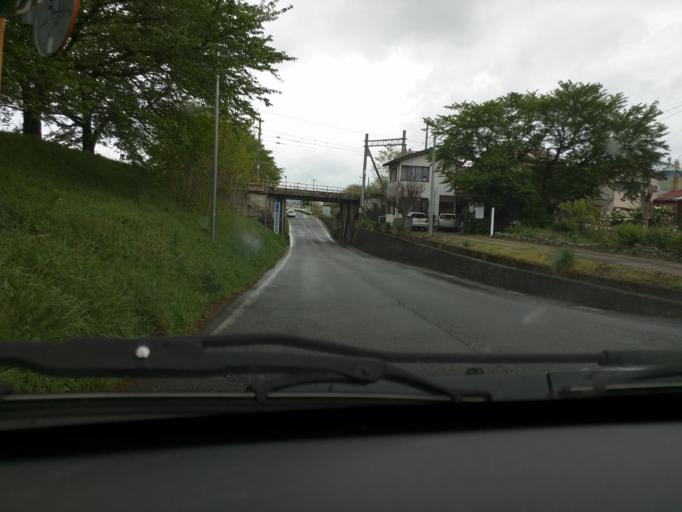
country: JP
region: Fukushima
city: Kitakata
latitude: 37.5916
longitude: 139.8879
